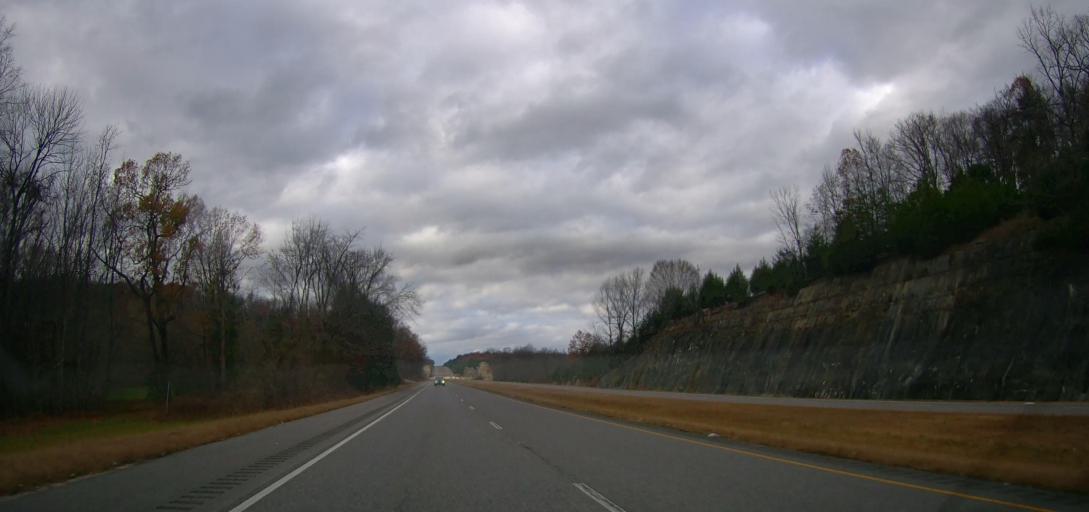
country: US
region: Alabama
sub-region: Lawrence County
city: Town Creek
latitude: 34.6058
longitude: -87.4512
